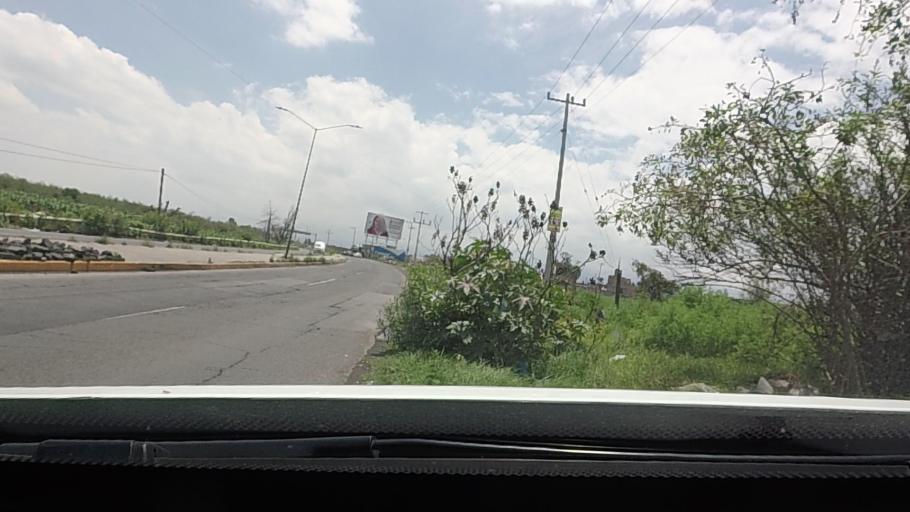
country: MX
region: Mexico
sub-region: Chalco
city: Barrio de Guadalupe
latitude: 19.2477
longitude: -98.9221
